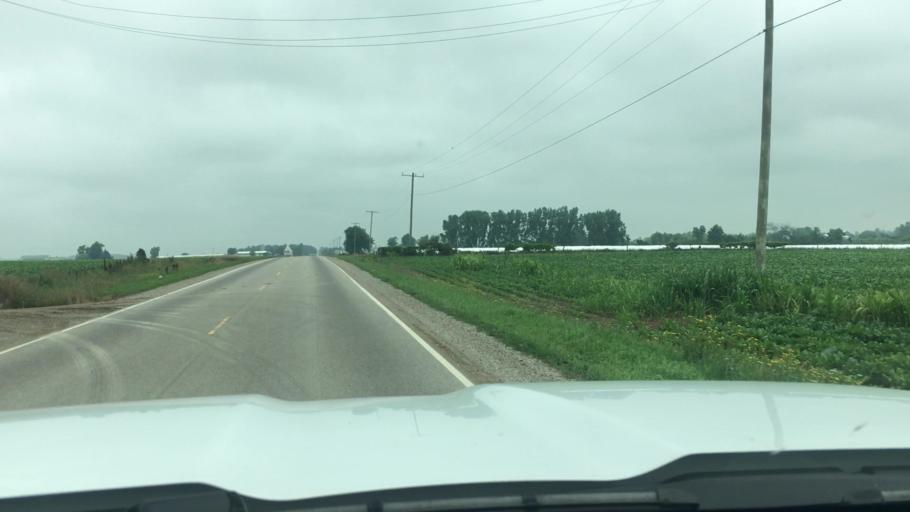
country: US
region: Michigan
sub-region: Sanilac County
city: Brown City
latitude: 43.2771
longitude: -82.9826
